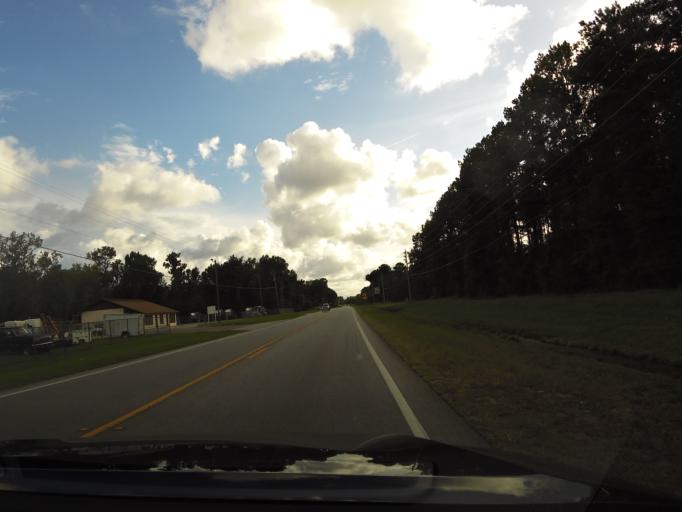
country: US
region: Georgia
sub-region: Liberty County
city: Midway
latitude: 31.7802
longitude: -81.4404
